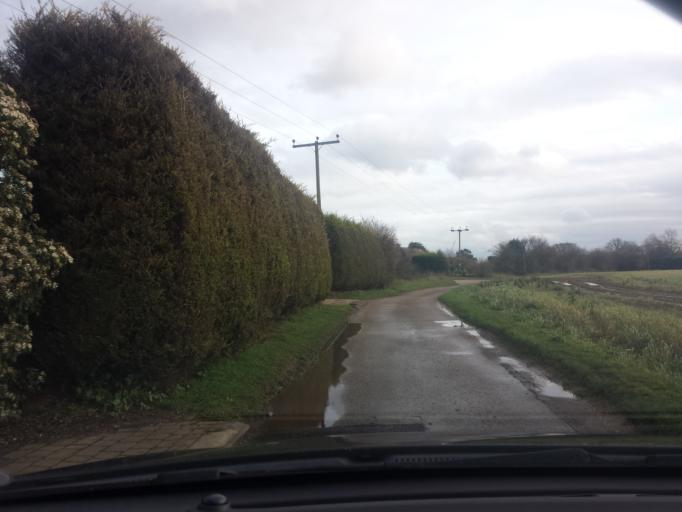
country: GB
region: England
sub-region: Essex
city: Great Bentley
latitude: 51.8928
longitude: 1.0521
